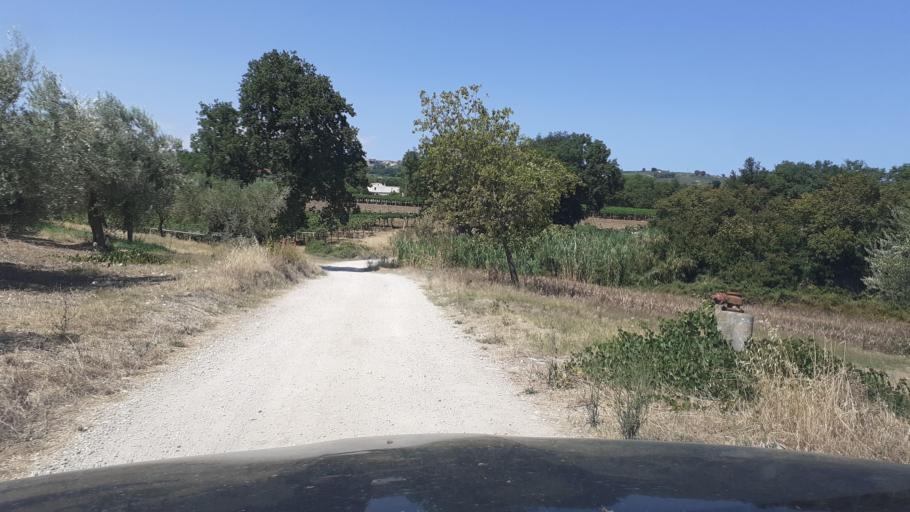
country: IT
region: Abruzzo
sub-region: Provincia di Chieti
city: Santa Maria Imbaro
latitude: 42.2073
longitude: 14.4780
